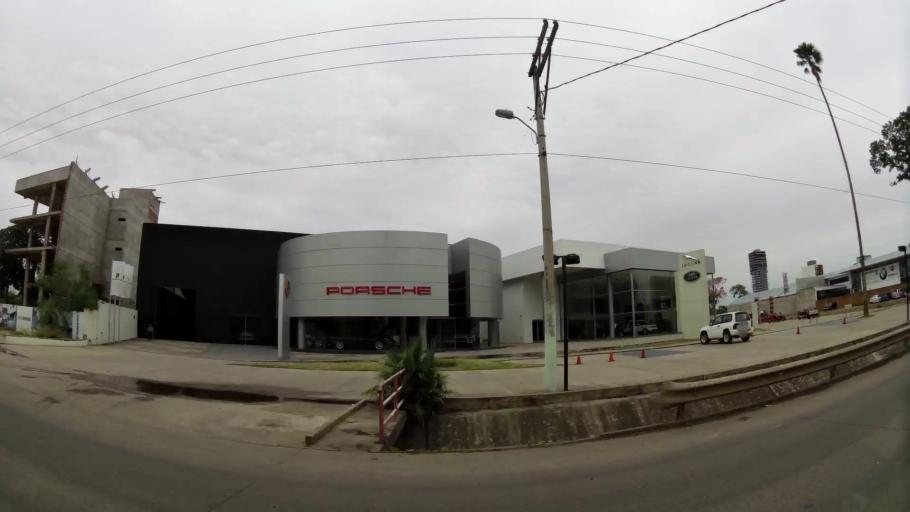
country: BO
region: Santa Cruz
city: Santa Cruz de la Sierra
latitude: -17.7608
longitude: -63.1927
